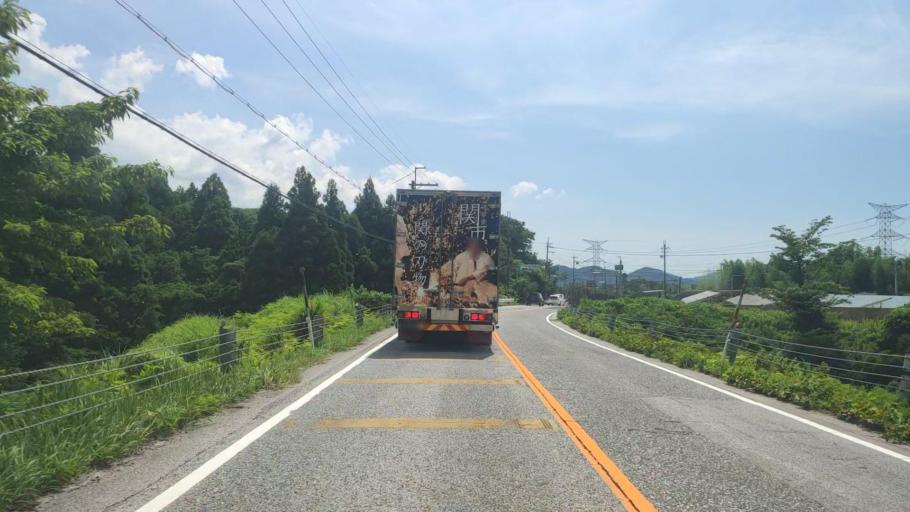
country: JP
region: Gifu
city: Tarui
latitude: 35.3702
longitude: 136.4035
